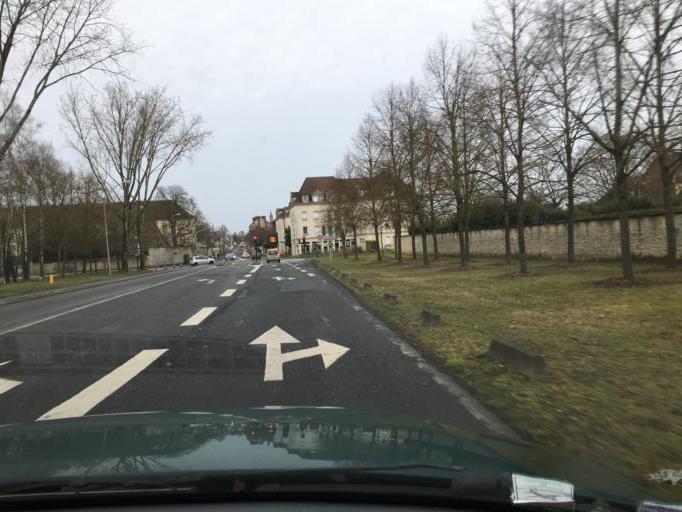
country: FR
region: Picardie
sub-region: Departement de l'Oise
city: Senlis
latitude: 49.1947
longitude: 2.5765
